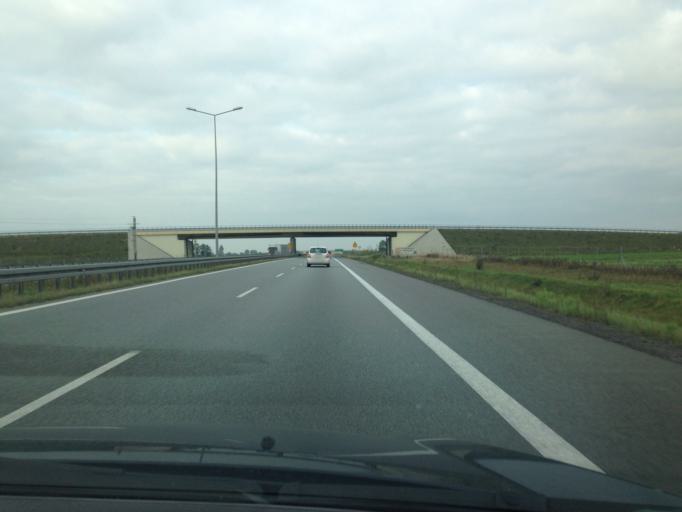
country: PL
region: Greater Poland Voivodeship
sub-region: Powiat poznanski
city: Kleszczewo
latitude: 52.3213
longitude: 17.1379
